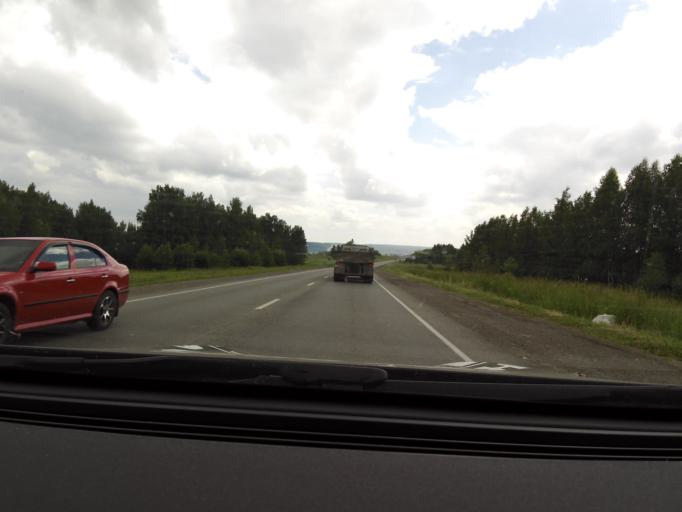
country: RU
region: Perm
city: Kungur
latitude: 57.3939
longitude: 56.9010
